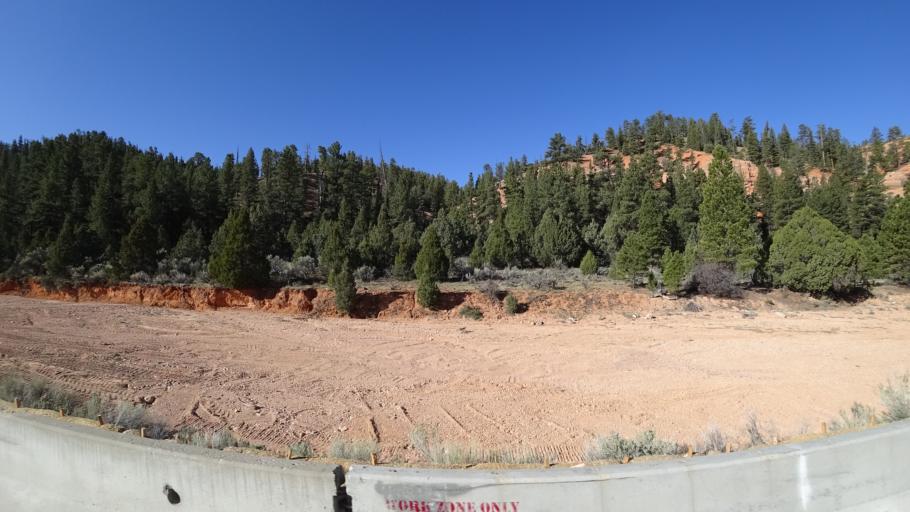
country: US
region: Utah
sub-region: Garfield County
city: Panguitch
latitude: 37.7406
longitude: -112.2991
